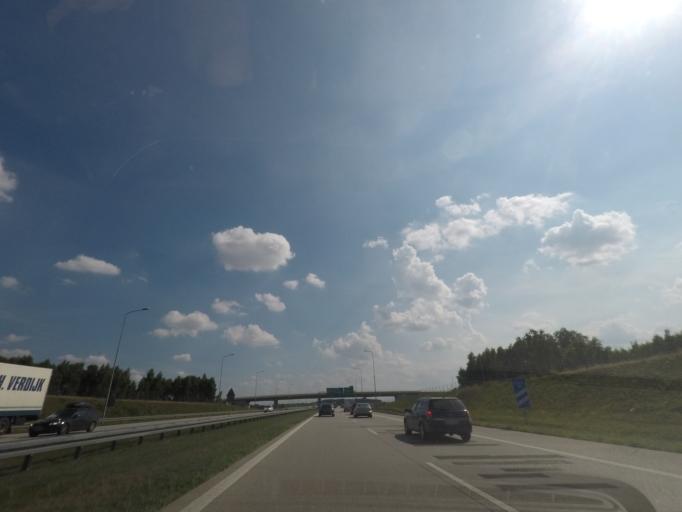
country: PL
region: Lodz Voivodeship
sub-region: Powiat piotrkowski
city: Czarnocin
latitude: 51.5570
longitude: 19.6040
